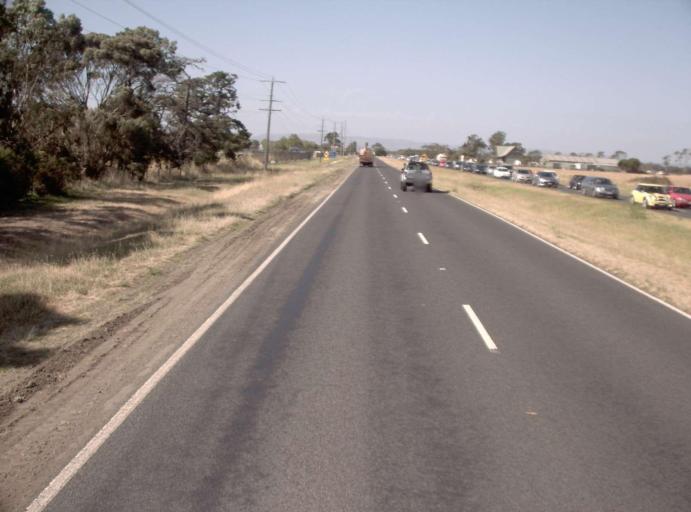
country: AU
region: Victoria
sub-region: Frankston
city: Sandhurst
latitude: -38.0686
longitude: 145.1975
